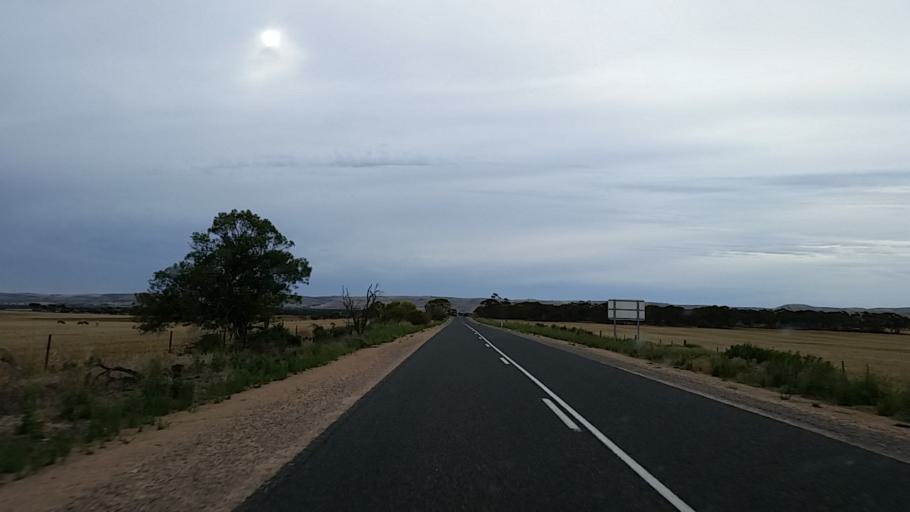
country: AU
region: South Australia
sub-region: Mid Murray
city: Mannum
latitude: -34.7554
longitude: 139.2778
